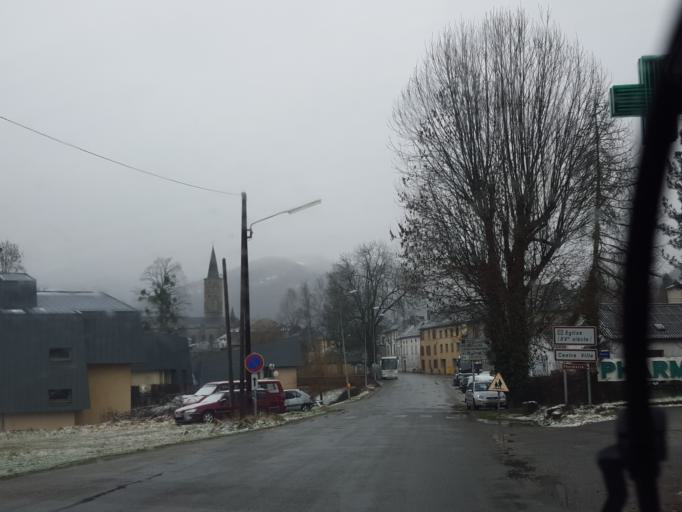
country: FR
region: Midi-Pyrenees
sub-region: Departement de l'Ariege
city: Saint-Girons
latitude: 42.8908
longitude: 1.3430
